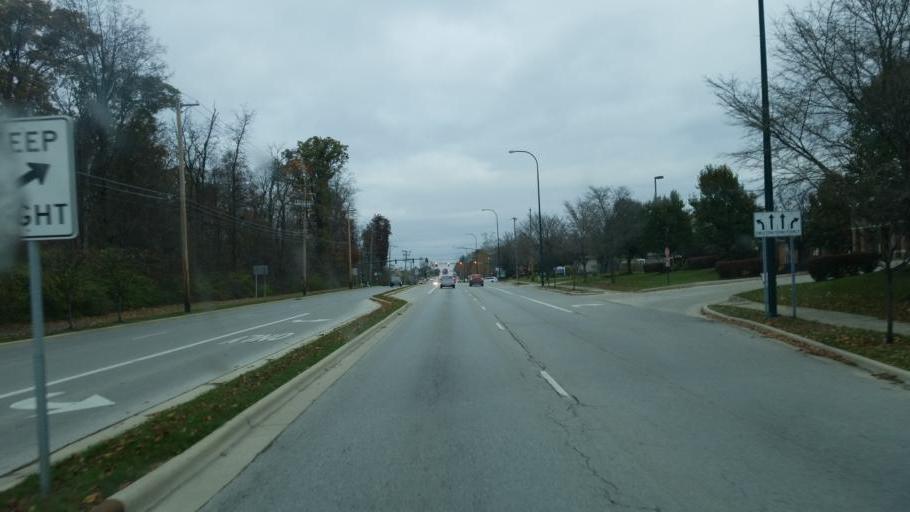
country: US
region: Ohio
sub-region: Franklin County
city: Gahanna
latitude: 40.0440
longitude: -82.8644
